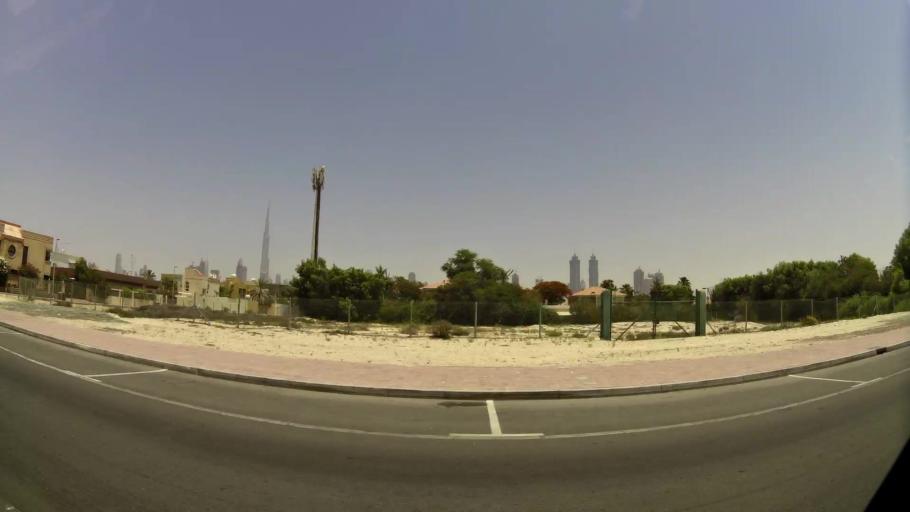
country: AE
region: Dubai
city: Dubai
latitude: 25.2012
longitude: 55.2431
